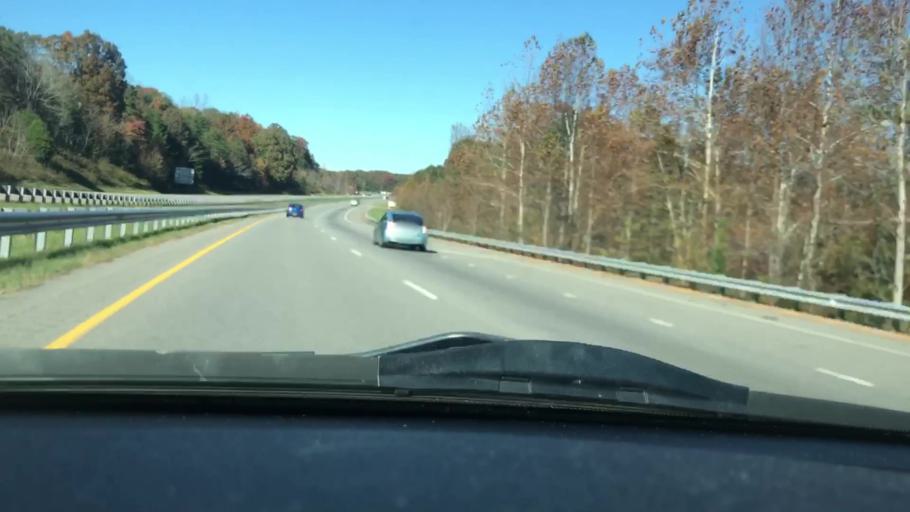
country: US
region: North Carolina
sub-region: Rockingham County
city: Stoneville
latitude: 36.4706
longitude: -79.9265
